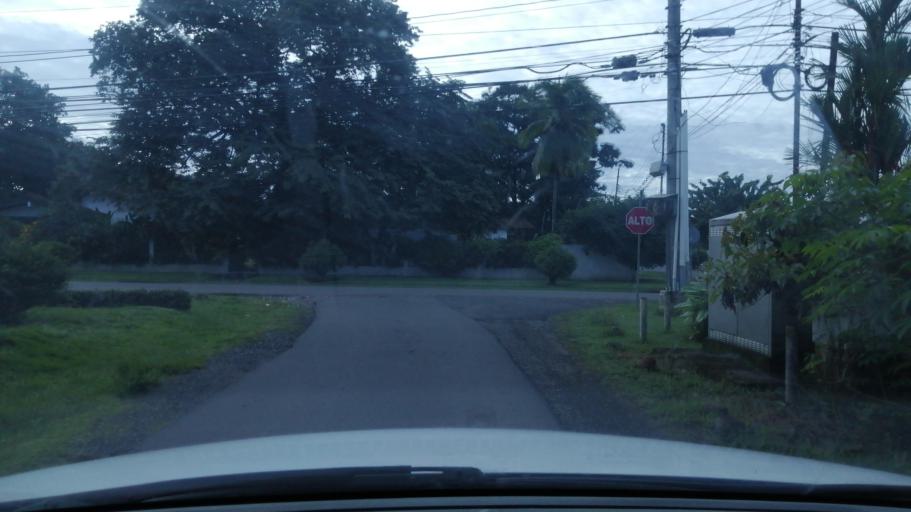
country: PA
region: Chiriqui
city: Mata del Nance
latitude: 8.4549
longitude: -82.4195
